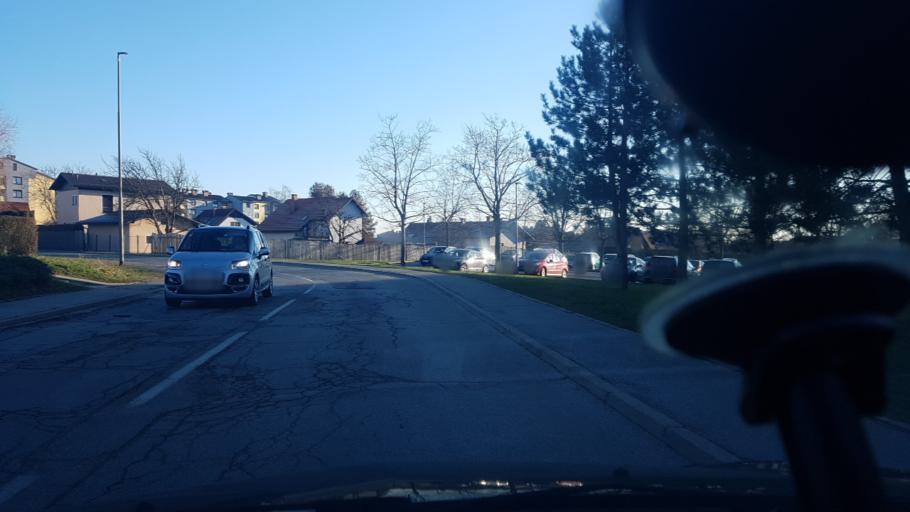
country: SI
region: Ptuj
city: Ptuj
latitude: 46.4291
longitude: 15.8716
